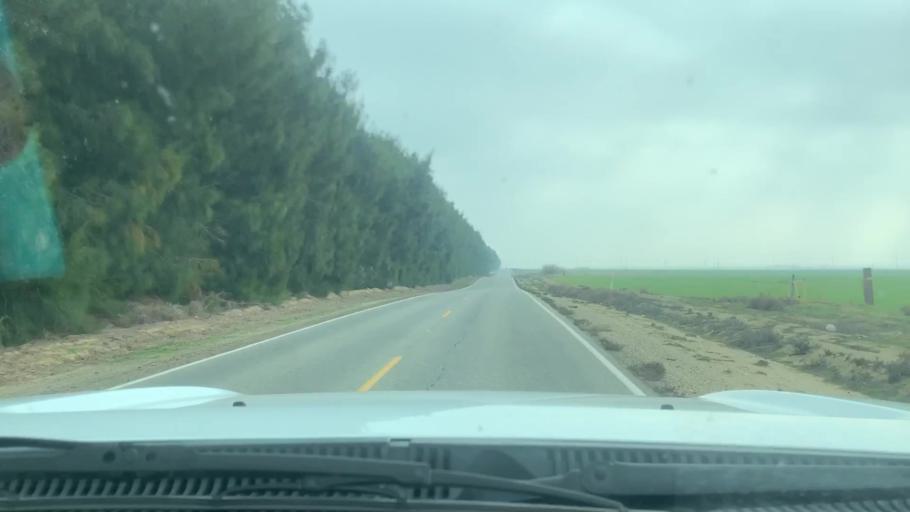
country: US
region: California
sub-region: Kern County
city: Lost Hills
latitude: 35.5097
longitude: -119.7475
